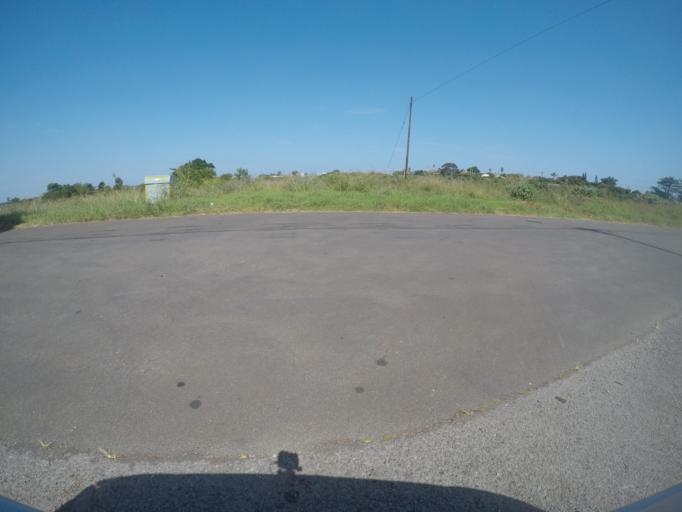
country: ZA
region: Eastern Cape
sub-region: Buffalo City Metropolitan Municipality
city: East London
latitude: -32.9697
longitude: 27.8784
